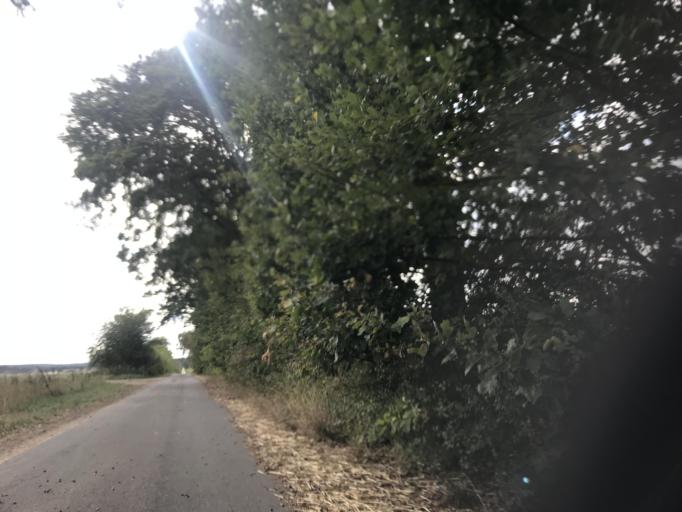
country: DE
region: Lower Saxony
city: Reinstorf
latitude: 53.2575
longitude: 10.5881
